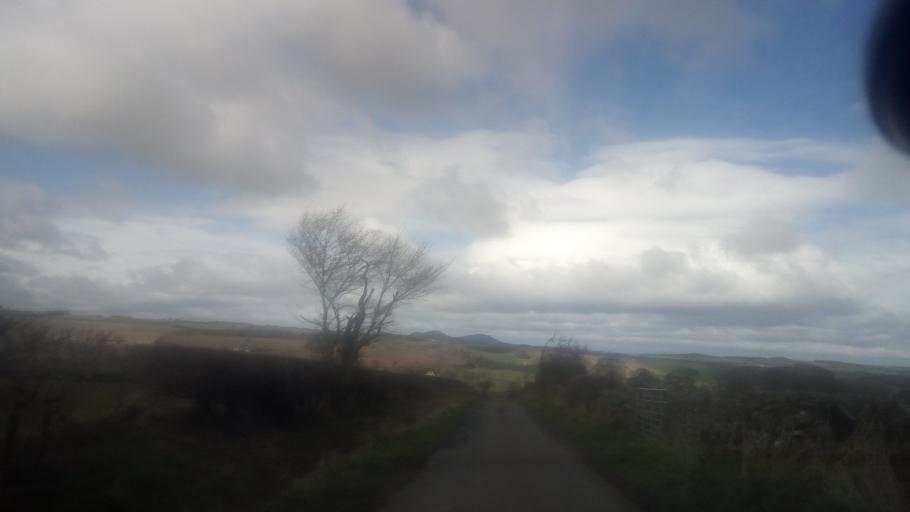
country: GB
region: Scotland
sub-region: The Scottish Borders
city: Jedburgh
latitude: 55.4819
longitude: -2.6064
